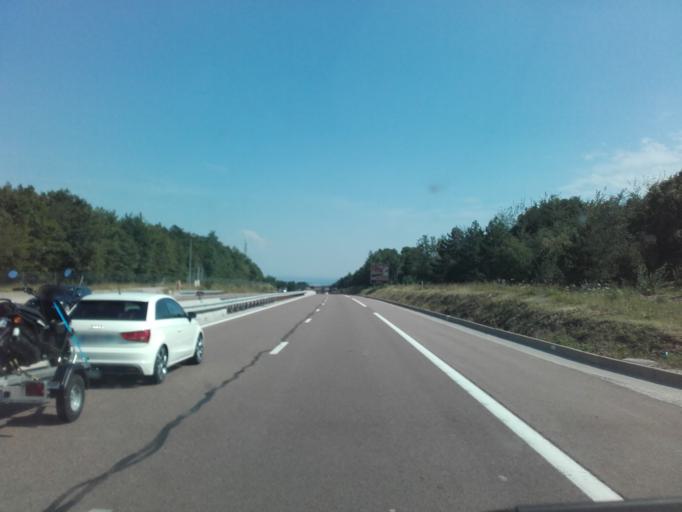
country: FR
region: Bourgogne
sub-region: Departement de la Cote-d'Or
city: Savigny-les-Beaune
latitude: 47.0663
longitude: 4.7675
